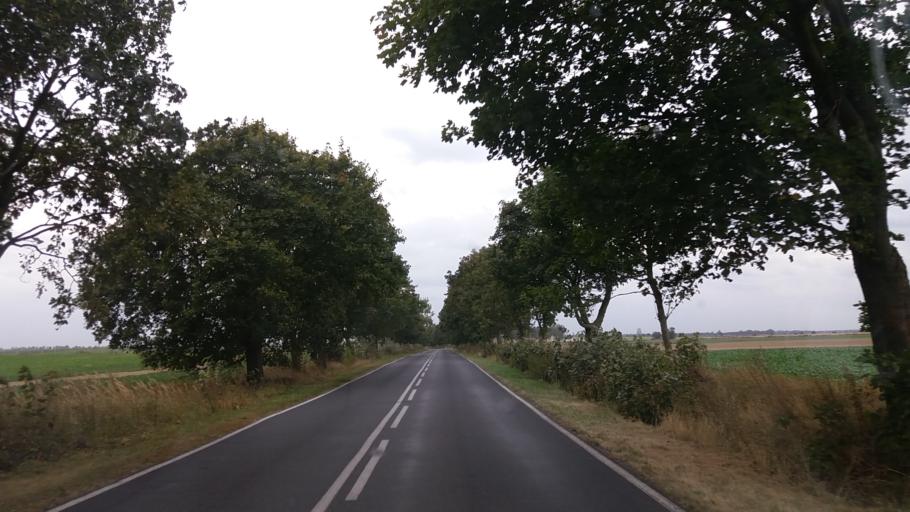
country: PL
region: Lubusz
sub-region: Powiat strzelecko-drezdenecki
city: Strzelce Krajenskie
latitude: 52.9125
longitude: 15.5596
